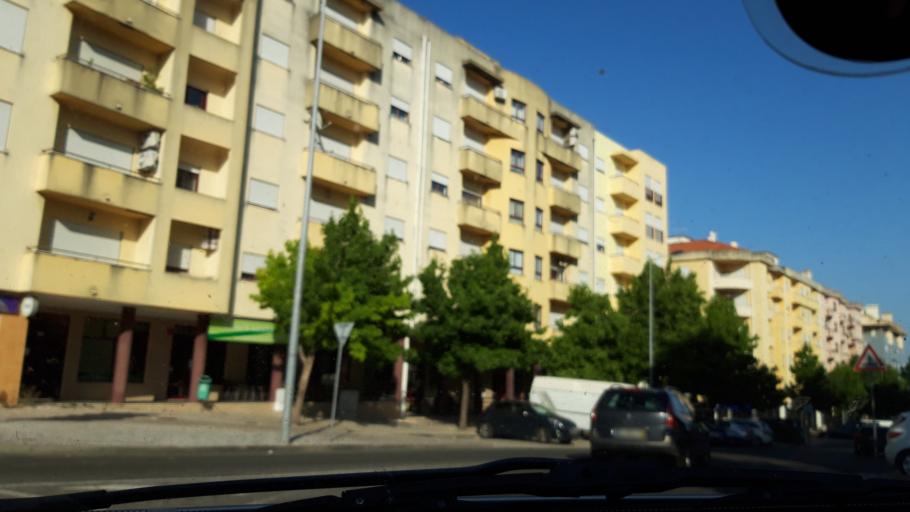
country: PT
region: Santarem
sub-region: Torres Novas
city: Torres Novas
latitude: 39.4765
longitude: -8.5500
